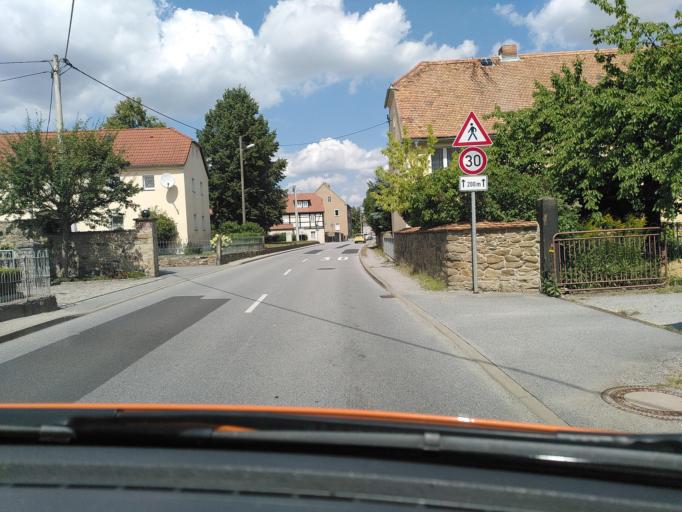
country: DE
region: Saxony
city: Grossdubrau
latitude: 51.2254
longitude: 14.4781
